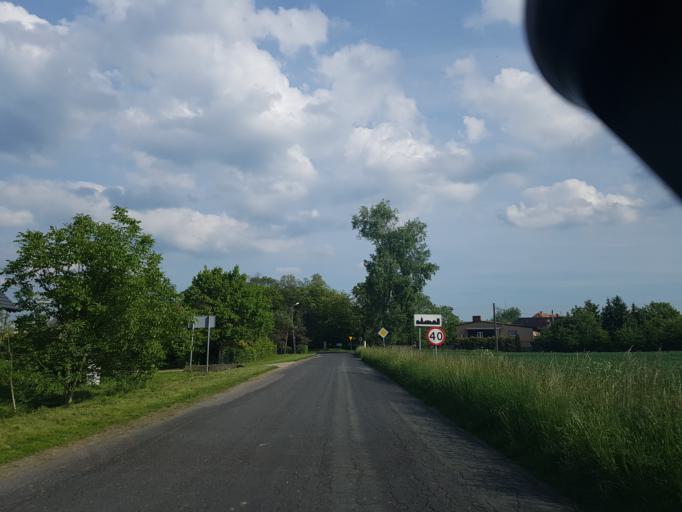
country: PL
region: Lower Silesian Voivodeship
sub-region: Powiat strzelinski
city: Wiazow
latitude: 50.8562
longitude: 17.1828
